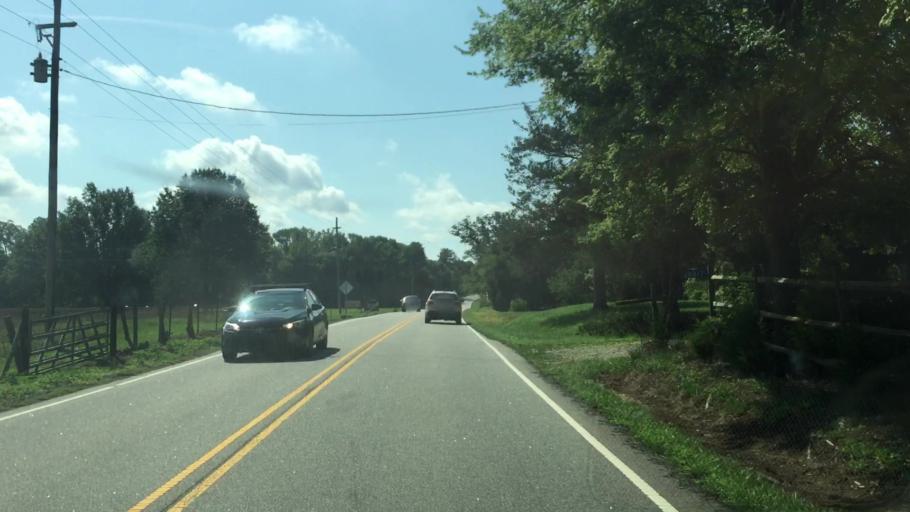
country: US
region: North Carolina
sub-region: Anson County
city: Burnsville
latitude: 35.0624
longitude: -80.2788
